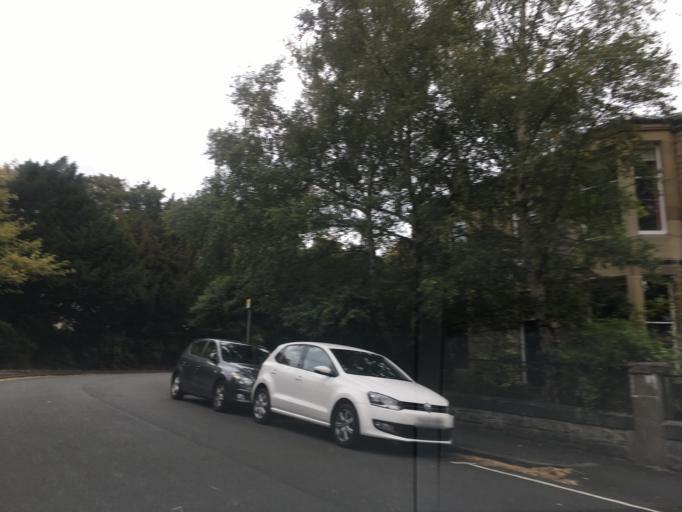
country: GB
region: Scotland
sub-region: Edinburgh
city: Edinburgh
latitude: 55.9341
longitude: -3.1683
